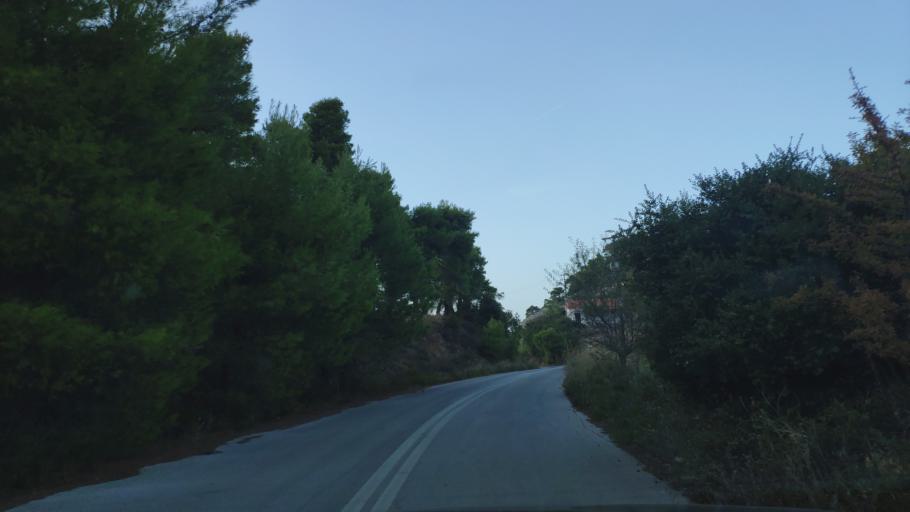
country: GR
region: West Greece
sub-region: Nomos Achaias
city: Aiyira
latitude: 38.0976
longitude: 22.4080
